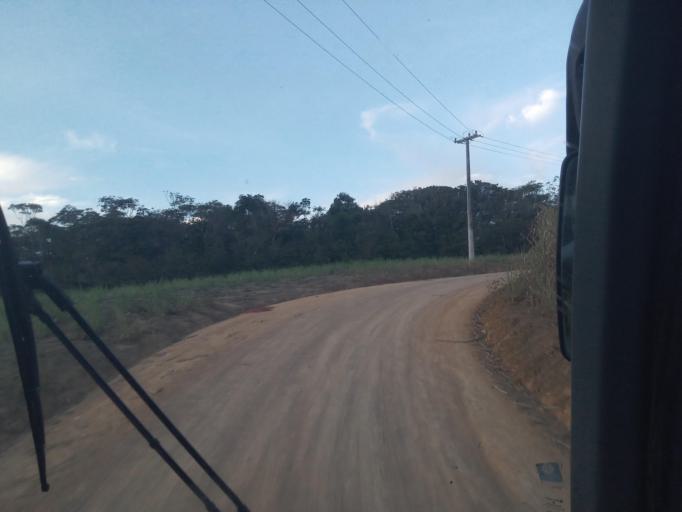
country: BR
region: Pernambuco
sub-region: Vitoria De Santo Antao
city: Vitoria de Santo Antao
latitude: -8.1592
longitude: -35.2578
